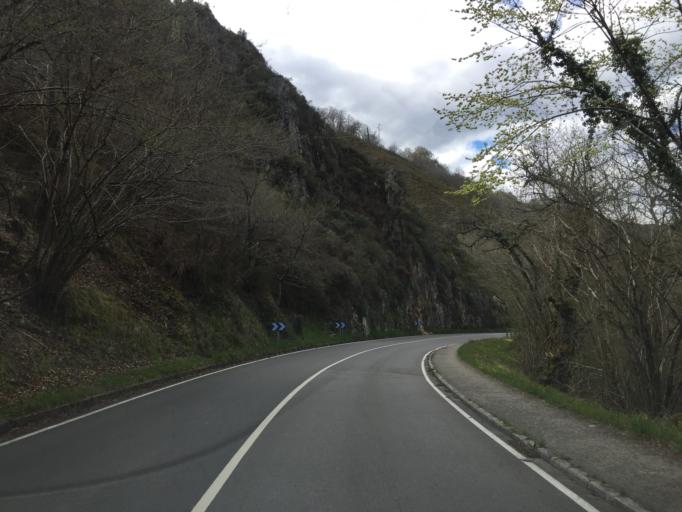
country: ES
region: Asturias
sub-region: Province of Asturias
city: Cangas de Onis
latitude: 43.3319
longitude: -5.0823
